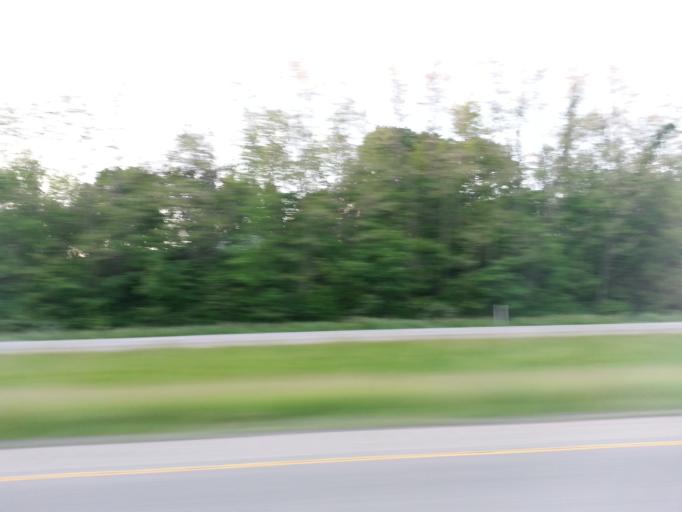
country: US
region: Indiana
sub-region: Fountain County
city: Veedersburg
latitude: 40.1195
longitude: -87.1700
